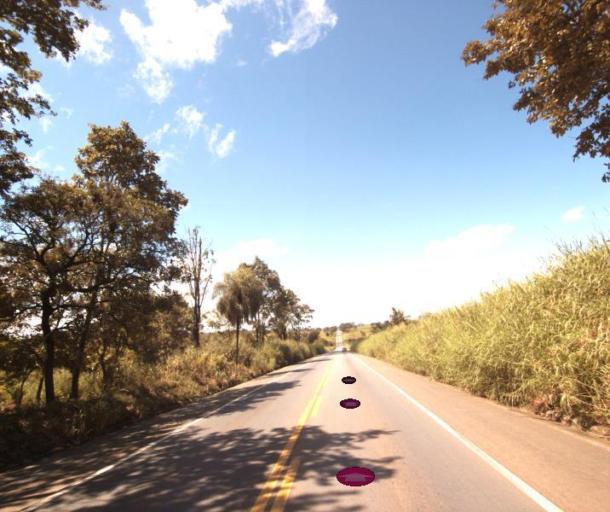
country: BR
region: Goias
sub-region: Jaragua
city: Jaragua
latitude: -15.8064
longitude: -49.2966
